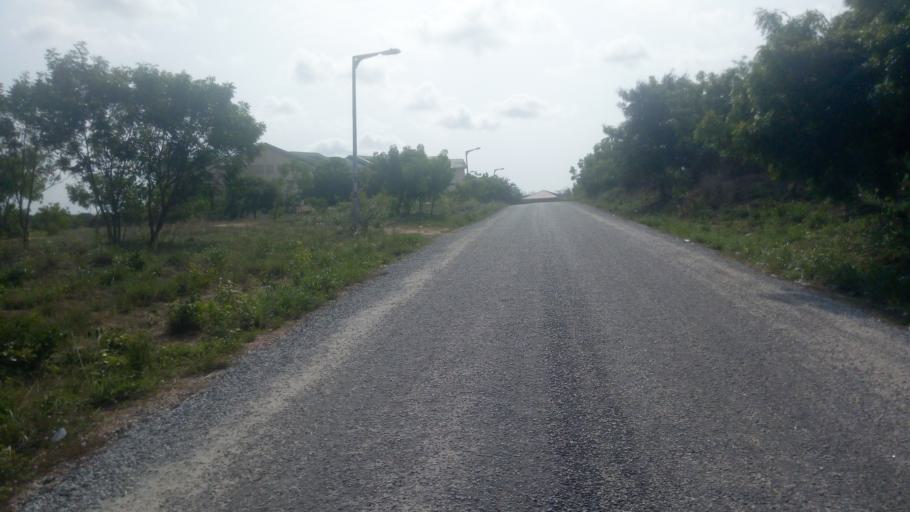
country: GH
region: Central
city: Winneba
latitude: 5.3792
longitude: -0.6235
